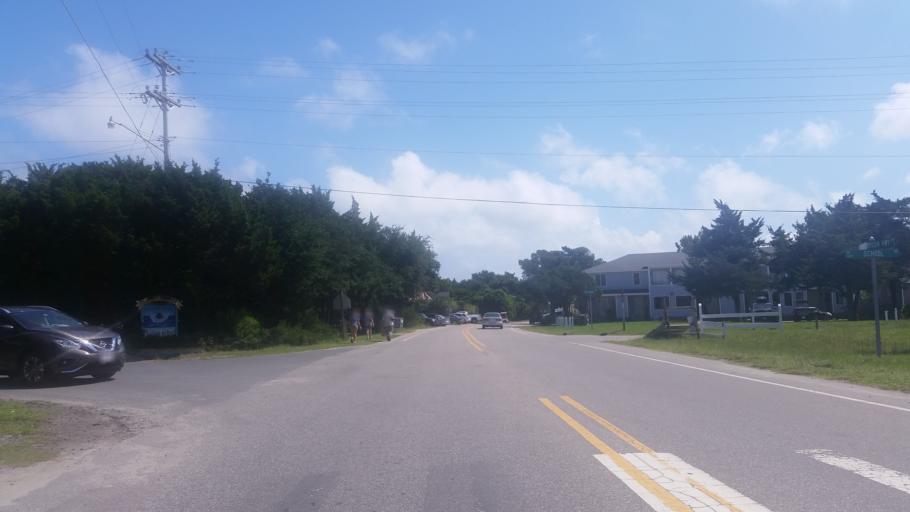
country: US
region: North Carolina
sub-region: Hyde County
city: Swanquarter
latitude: 35.1110
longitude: -75.9803
